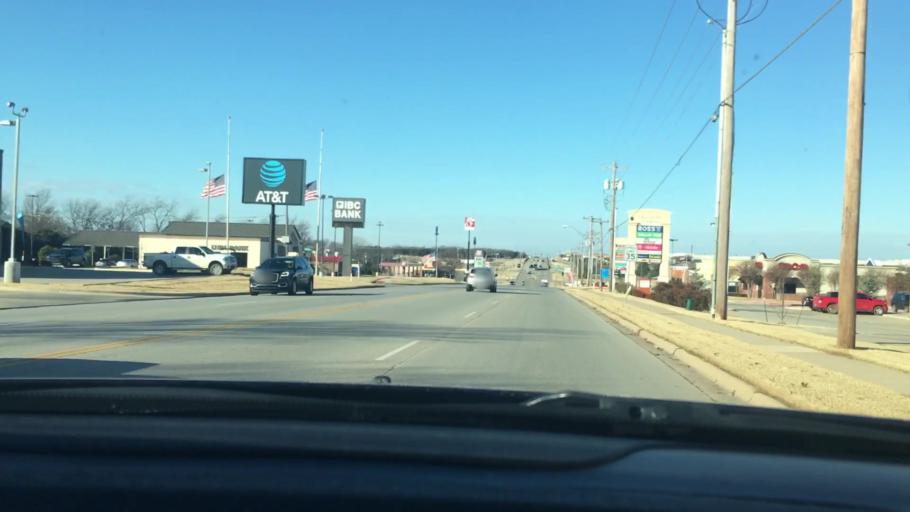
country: US
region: Oklahoma
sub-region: Carter County
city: Ardmore
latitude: 34.1875
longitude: -97.1573
